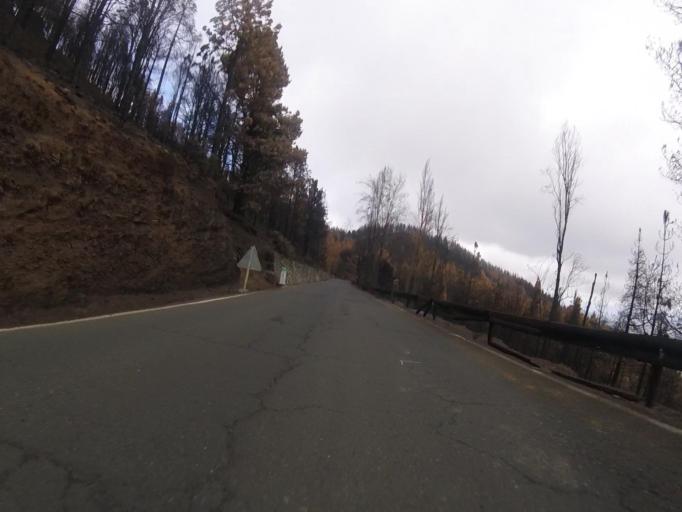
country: ES
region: Canary Islands
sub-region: Provincia de Las Palmas
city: Tejeda
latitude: 27.9795
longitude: -15.5797
